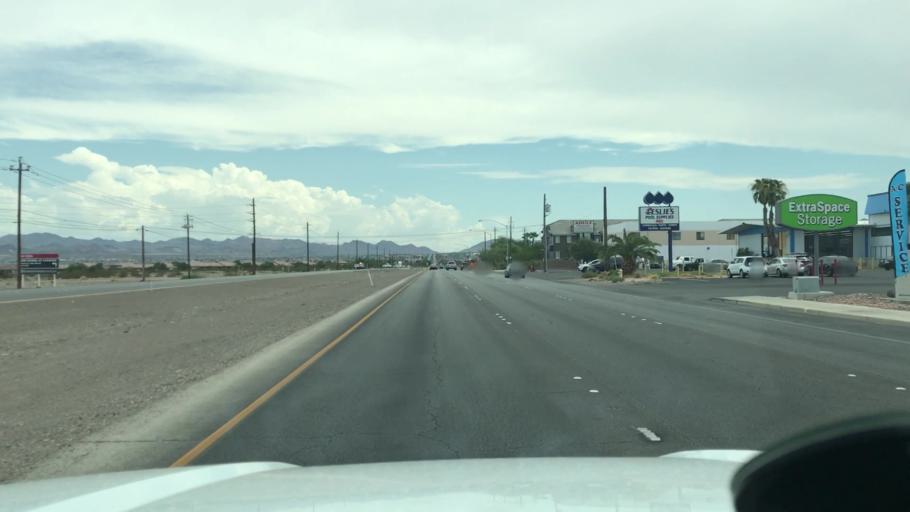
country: US
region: Nevada
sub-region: Clark County
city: Whitney
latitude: 36.0790
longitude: -115.0265
